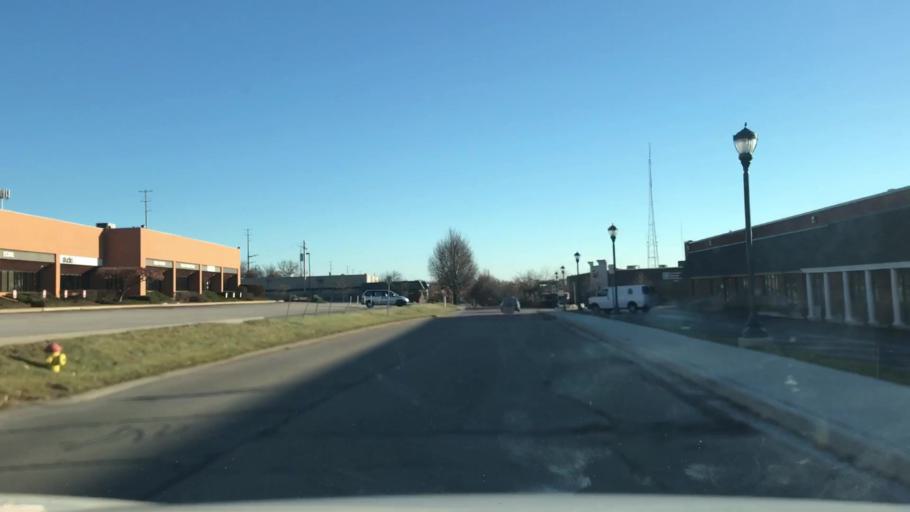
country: US
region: Missouri
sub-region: Saint Louis County
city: Brentwood
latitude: 38.6234
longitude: -90.3382
